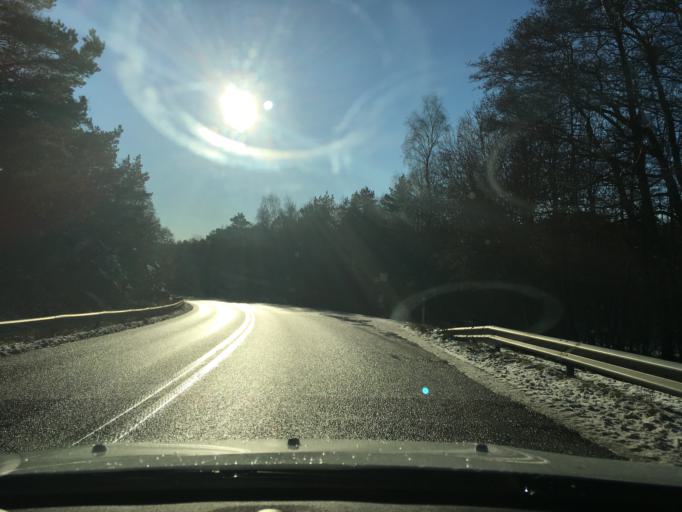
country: SE
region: Vaestra Goetaland
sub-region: Tjorns Kommun
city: Myggenas
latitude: 58.0824
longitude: 11.6948
